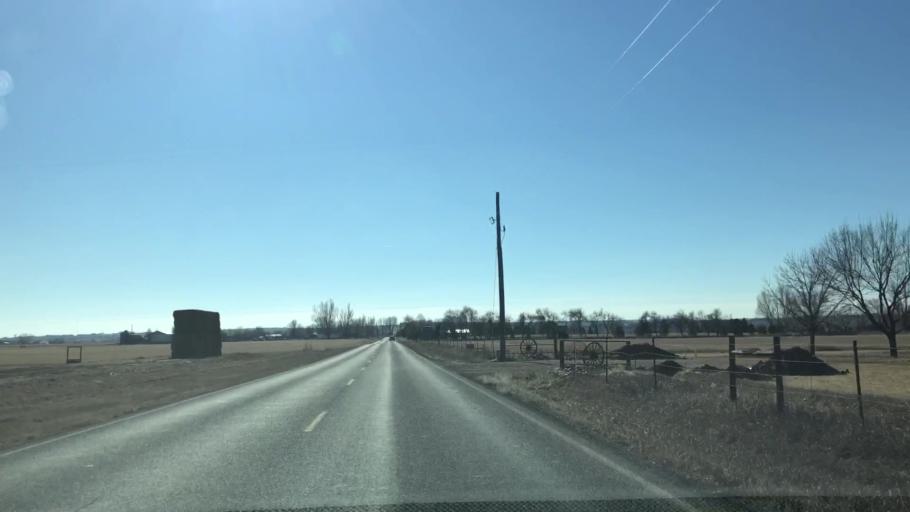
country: US
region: Colorado
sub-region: Weld County
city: Windsor
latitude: 40.4965
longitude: -104.9442
